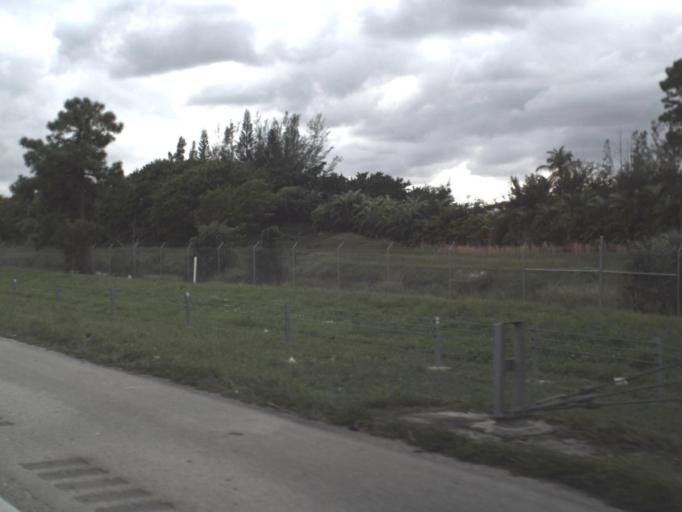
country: US
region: Florida
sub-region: Palm Beach County
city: Lake Belvedere Estates
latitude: 26.6591
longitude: -80.1743
